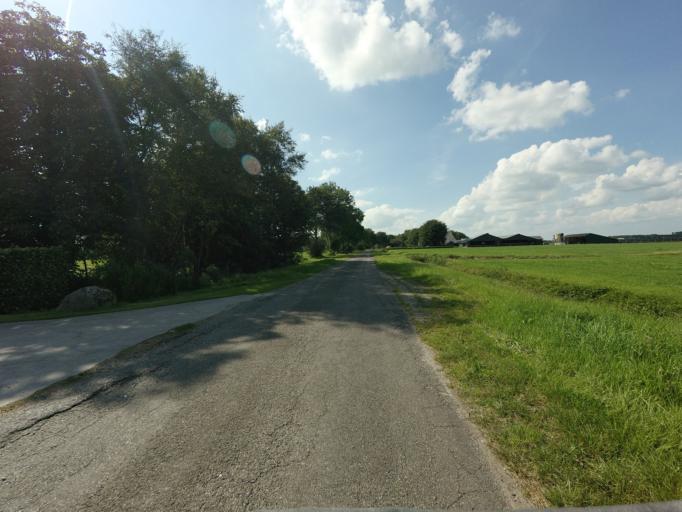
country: NL
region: Friesland
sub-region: Gemeente Heerenveen
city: Jubbega
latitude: 52.9802
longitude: 6.2578
